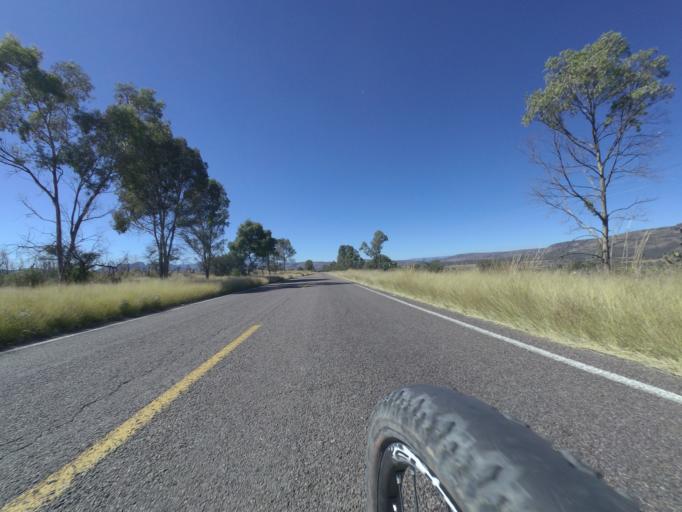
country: MX
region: Aguascalientes
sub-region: Aguascalientes
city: Los Canos
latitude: 21.8643
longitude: -102.5052
